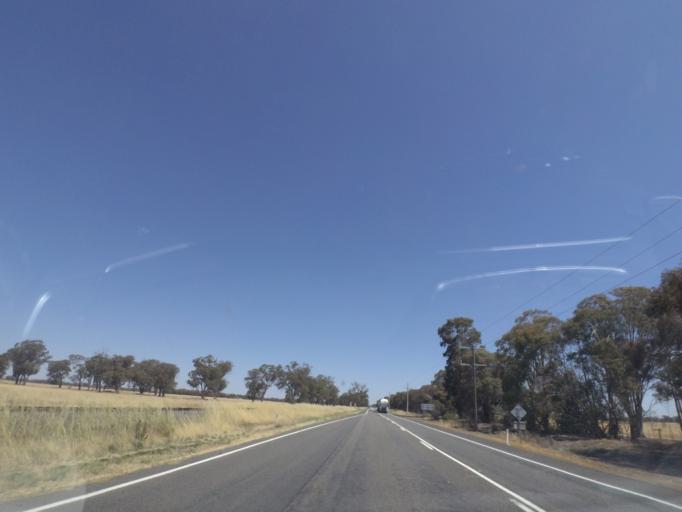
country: AU
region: Victoria
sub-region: Greater Shepparton
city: Shepparton
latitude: -36.1997
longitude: 145.4318
